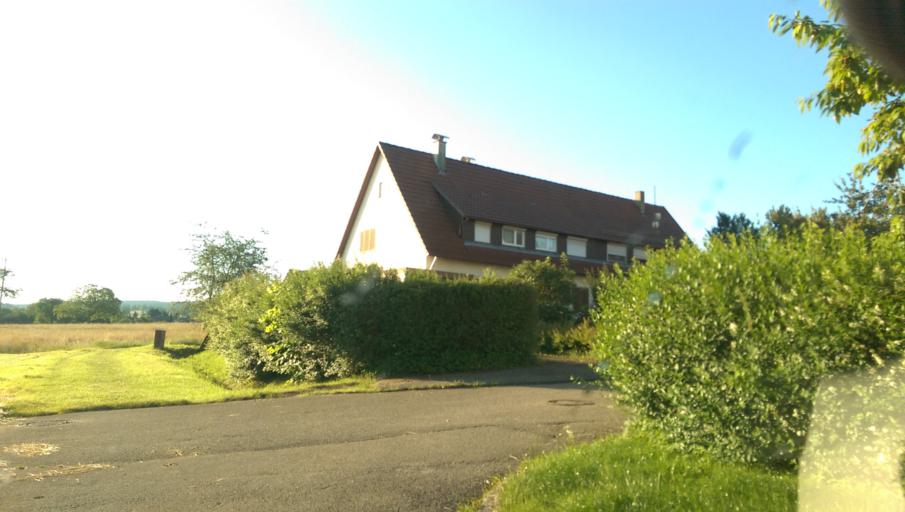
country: DE
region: Baden-Wuerttemberg
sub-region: Karlsruhe Region
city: Dobel
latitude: 48.8568
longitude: 8.5192
